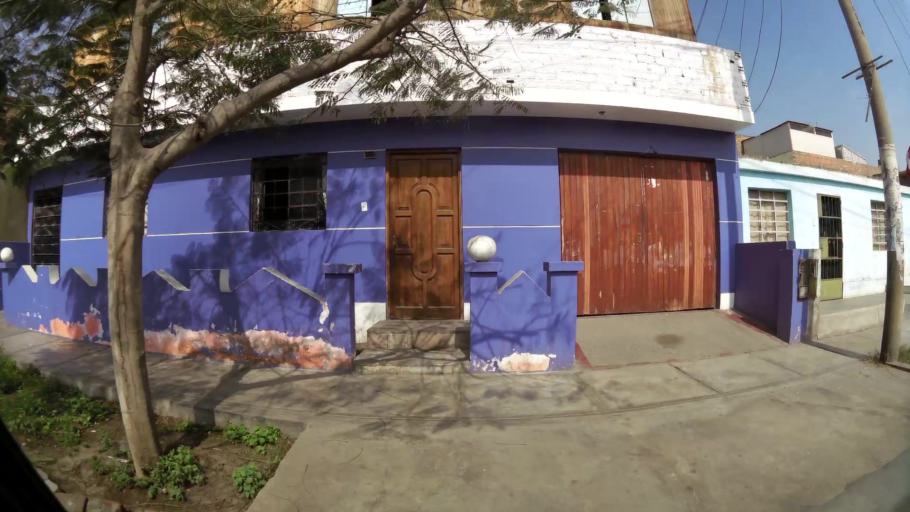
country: PE
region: Lima
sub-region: Lima
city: Santa Rosa
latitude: -11.7801
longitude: -77.1617
